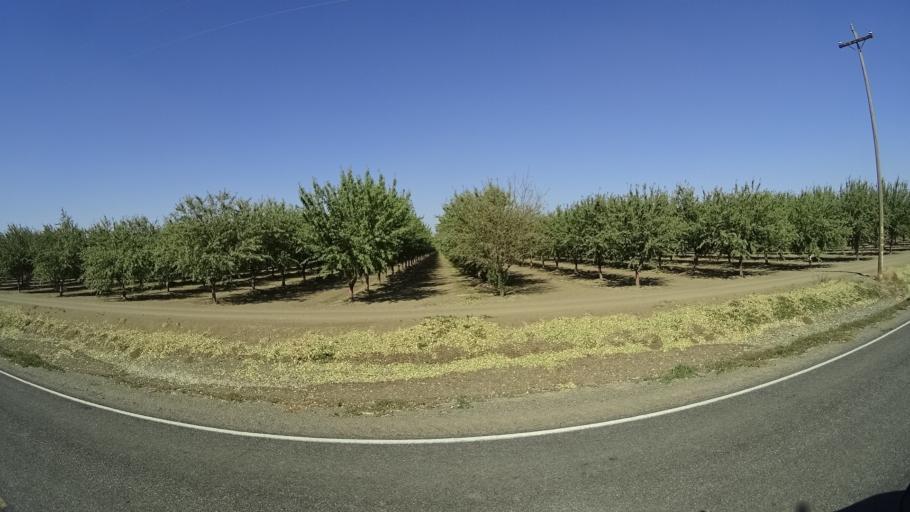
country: US
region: California
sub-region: Yolo County
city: Davis
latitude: 38.5906
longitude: -121.8232
